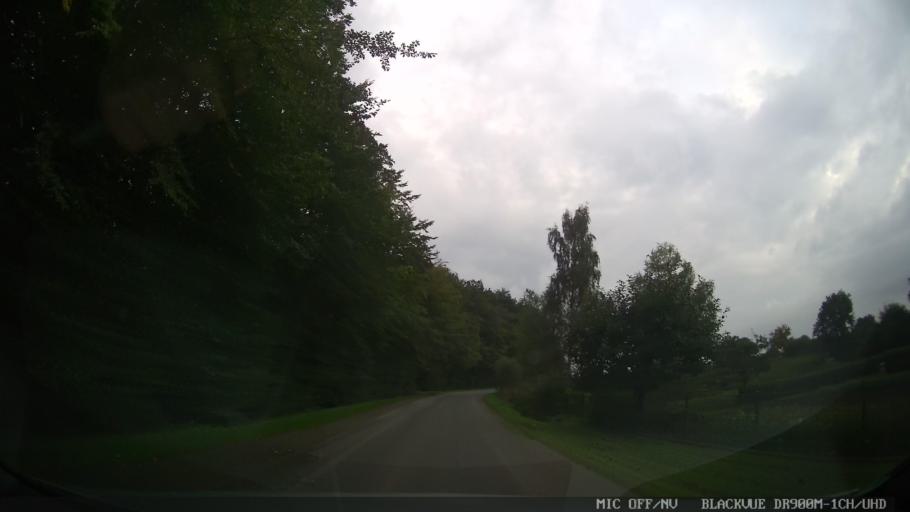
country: DE
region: Schleswig-Holstein
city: Gromitz
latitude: 54.1799
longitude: 10.9681
